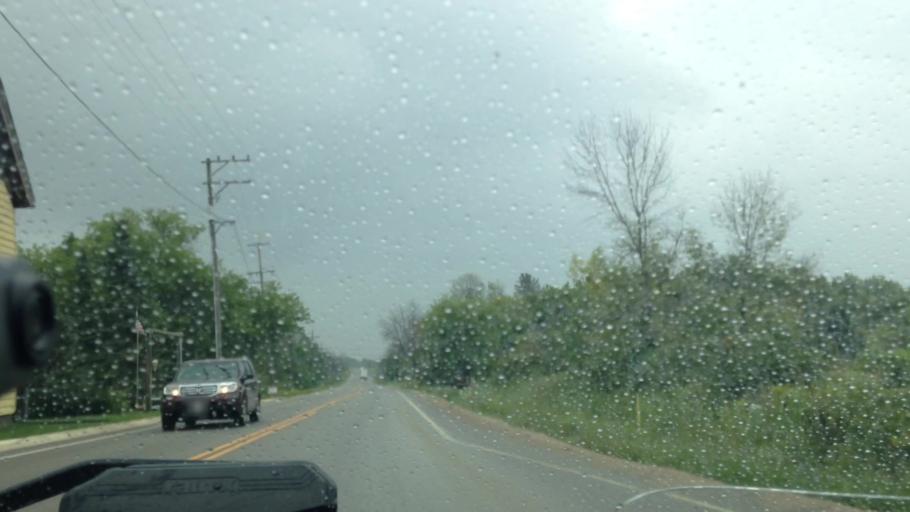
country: US
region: Wisconsin
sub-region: Washington County
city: Richfield
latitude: 43.2917
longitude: -88.2186
